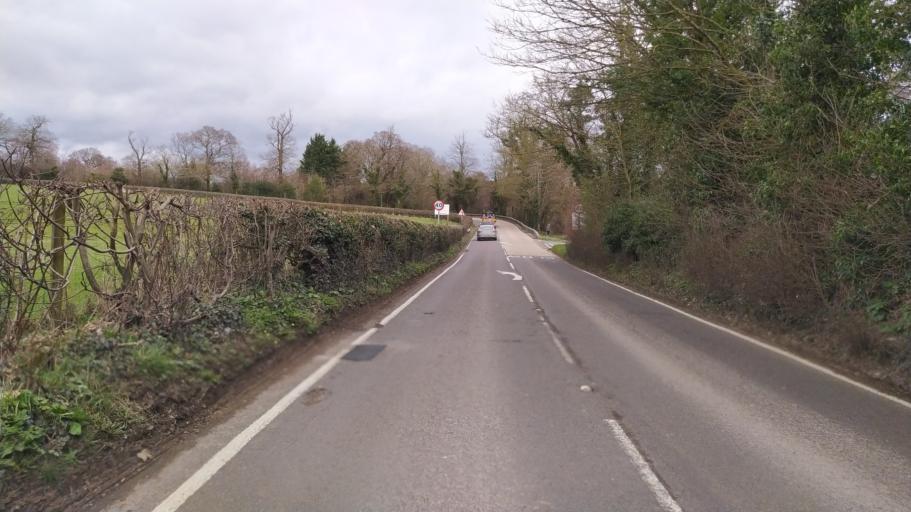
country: GB
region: England
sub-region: Surrey
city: Farnham
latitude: 51.2205
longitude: -0.8029
